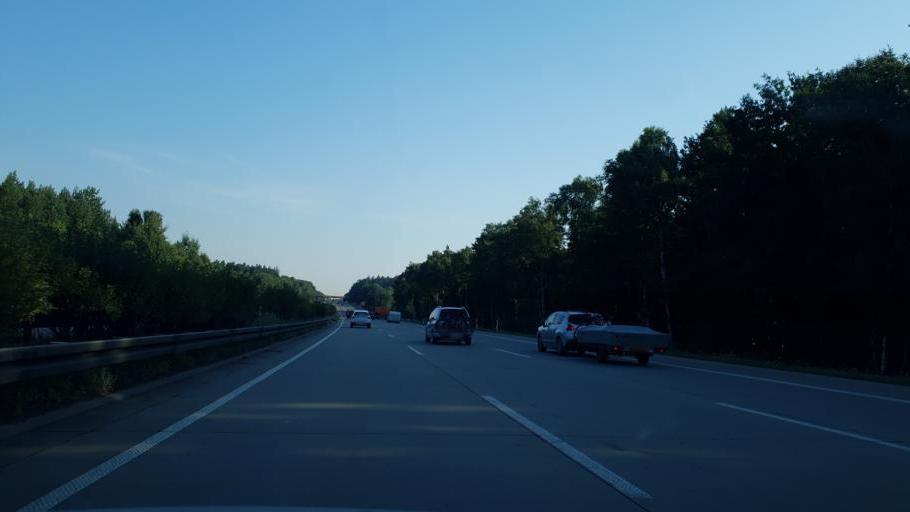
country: DE
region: Thuringia
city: Bad Klosterlausnitz
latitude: 50.9219
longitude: 11.8400
